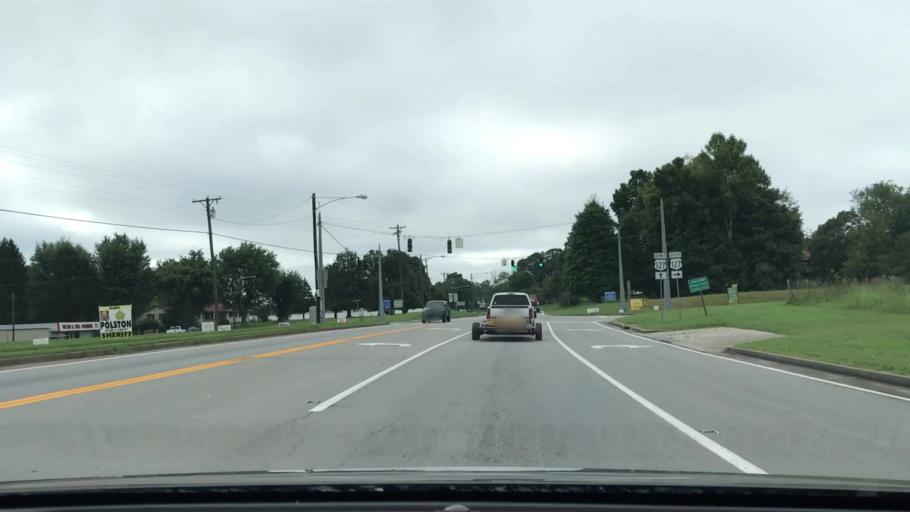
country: US
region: Kentucky
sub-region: Russell County
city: Jamestown
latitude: 36.9992
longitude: -85.0725
